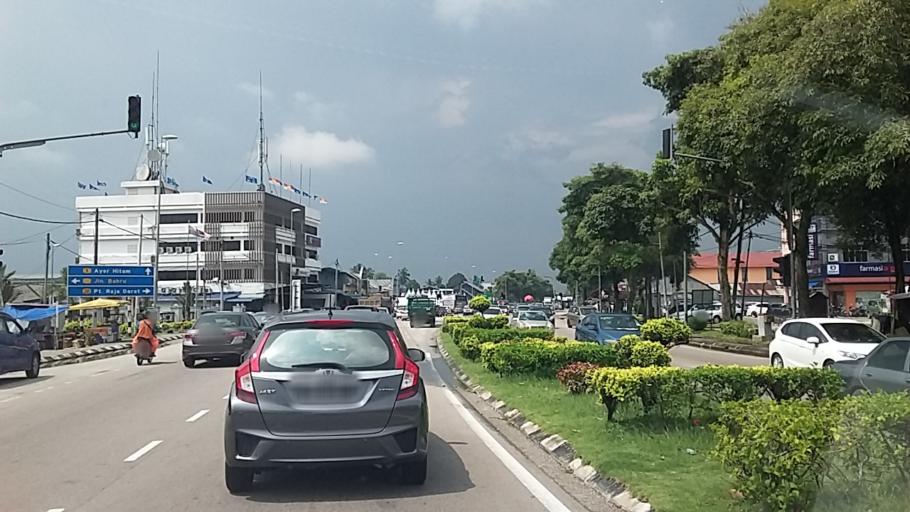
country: MY
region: Johor
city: Parit Raja
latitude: 1.8649
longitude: 103.1106
